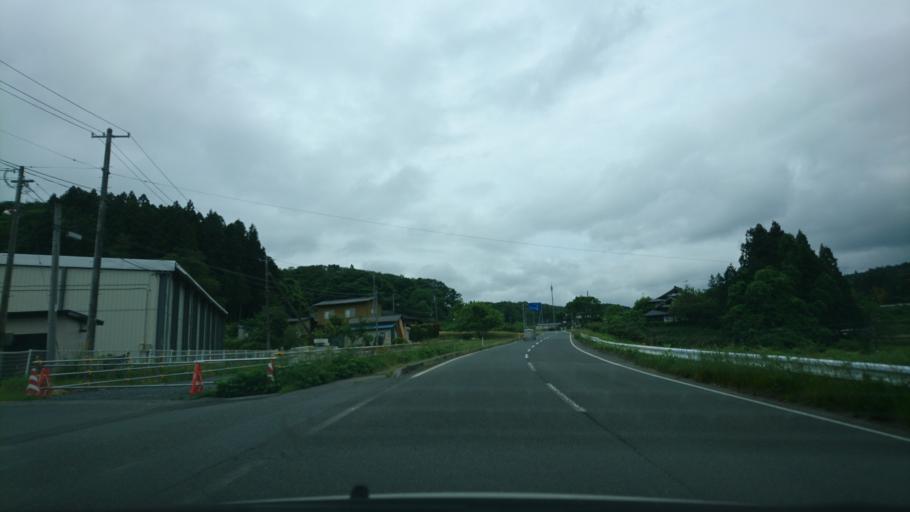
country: JP
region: Iwate
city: Ichinoseki
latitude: 38.8910
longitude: 141.1207
